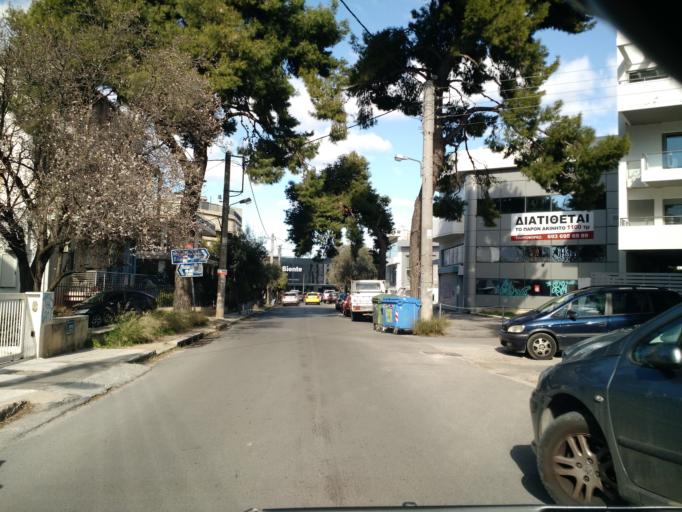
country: GR
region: Attica
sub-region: Nomarchia Athinas
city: Agia Paraskevi
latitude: 38.0122
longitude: 23.8333
